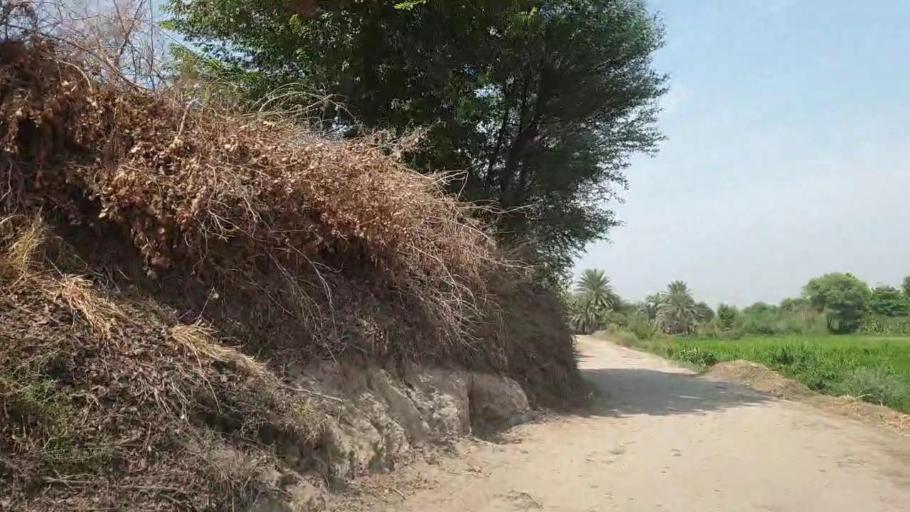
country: PK
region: Sindh
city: Pir jo Goth
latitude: 27.5501
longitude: 68.5172
